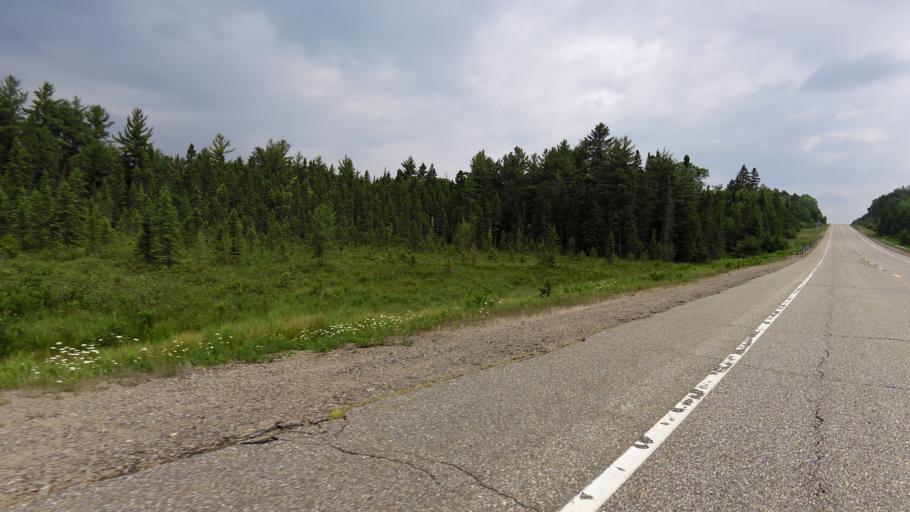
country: CA
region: Ontario
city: Huntsville
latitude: 45.5611
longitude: -78.5754
